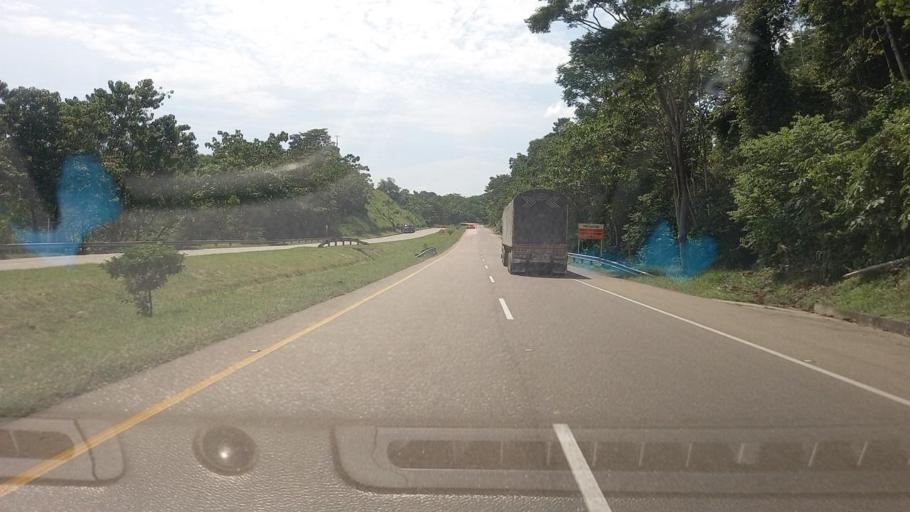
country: CO
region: Antioquia
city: Puerto Berrio
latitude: 6.3753
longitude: -74.4051
